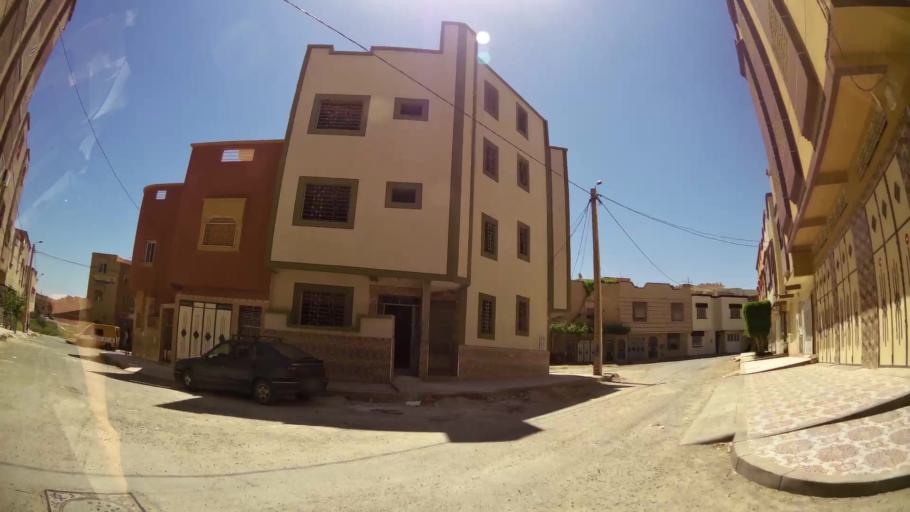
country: MA
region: Oriental
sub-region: Oujda-Angad
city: Oujda
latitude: 34.6576
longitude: -1.8829
